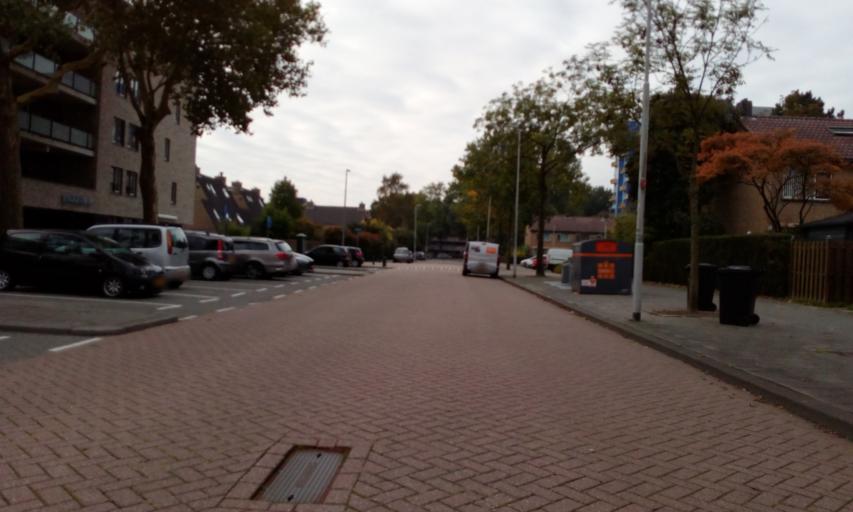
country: NL
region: South Holland
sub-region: Gemeente Spijkenisse
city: Spijkenisse
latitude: 51.8525
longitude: 4.3635
